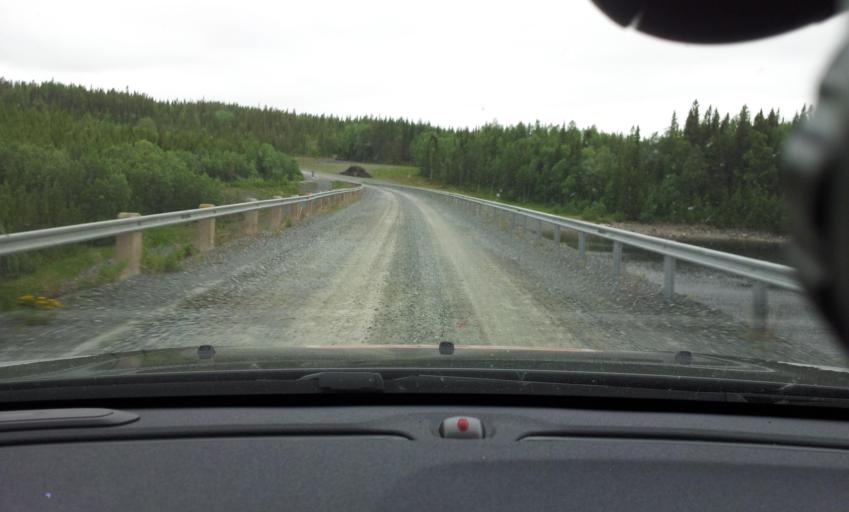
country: SE
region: Jaemtland
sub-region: Are Kommun
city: Jarpen
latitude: 63.1869
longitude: 13.6226
